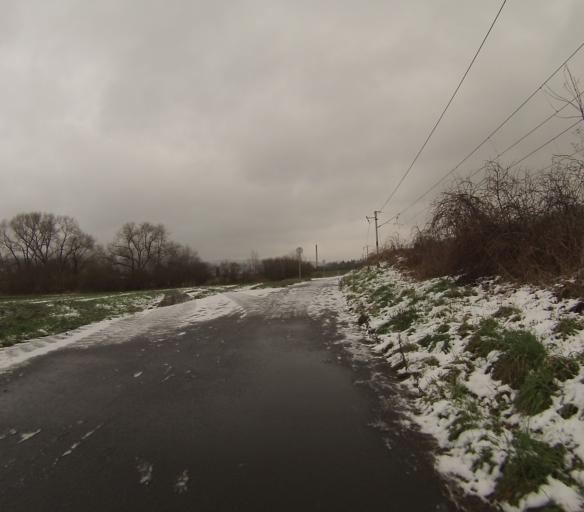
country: CZ
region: Ustecky
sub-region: Okres Decin
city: Decin
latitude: 50.7523
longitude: 14.1963
